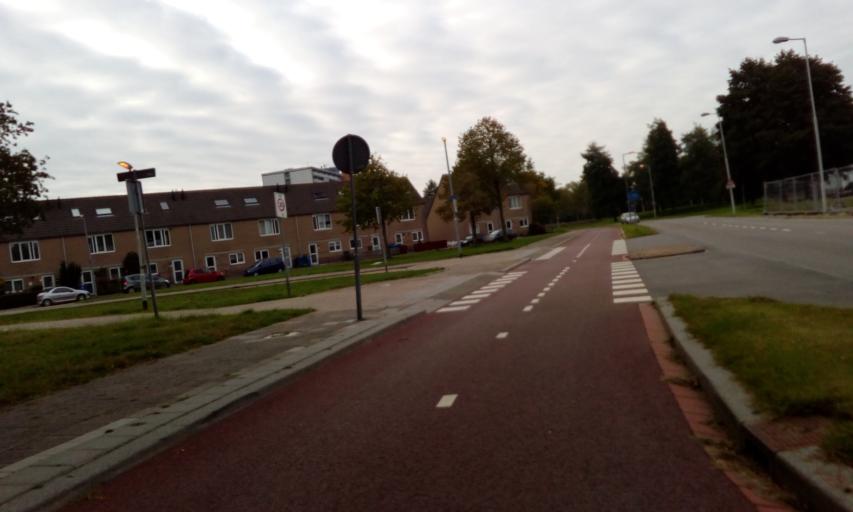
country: NL
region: South Holland
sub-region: Gemeente Spijkenisse
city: Spijkenisse
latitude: 51.8586
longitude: 4.3666
